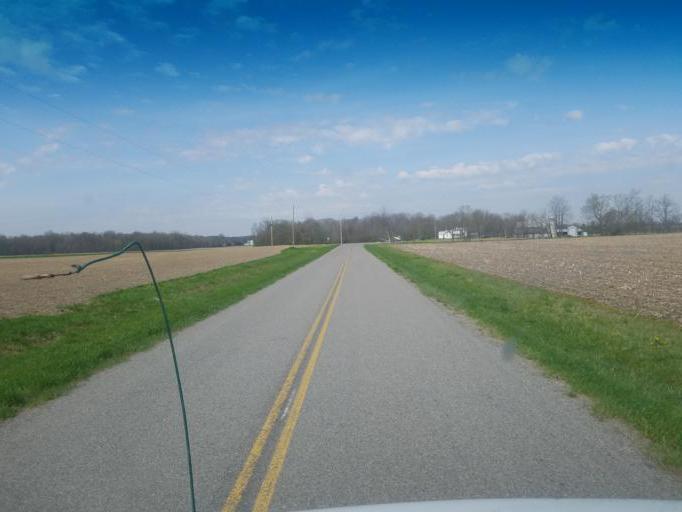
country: US
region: Ohio
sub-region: Logan County
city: Northwood
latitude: 40.4930
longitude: -83.6188
